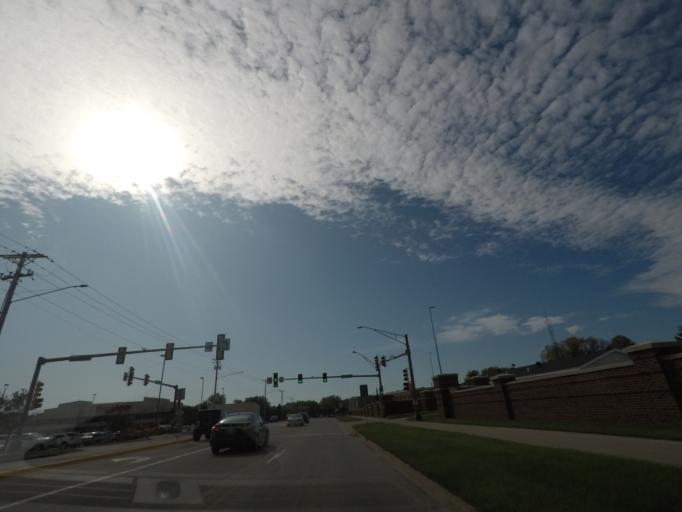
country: US
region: Iowa
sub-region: Story County
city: Ames
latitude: 42.0217
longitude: -93.6203
